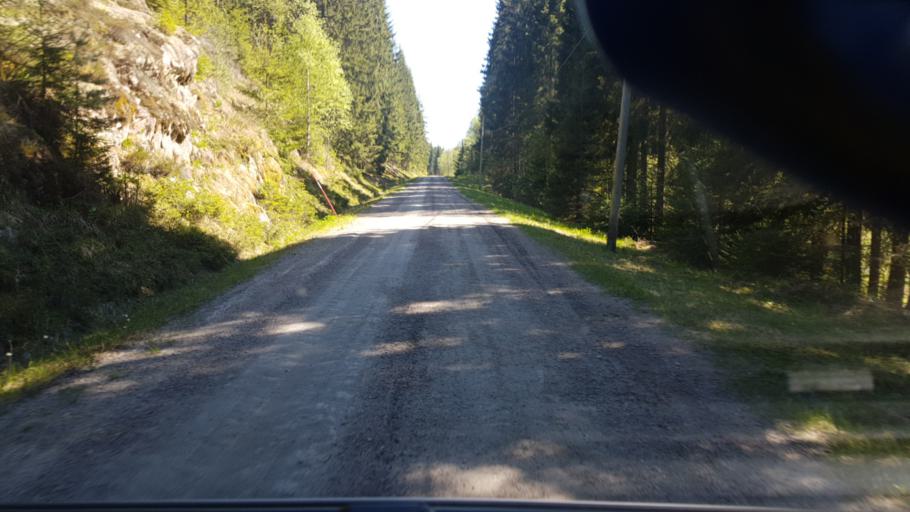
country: SE
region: Vaermland
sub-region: Eda Kommun
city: Charlottenberg
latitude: 59.9267
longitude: 12.3750
